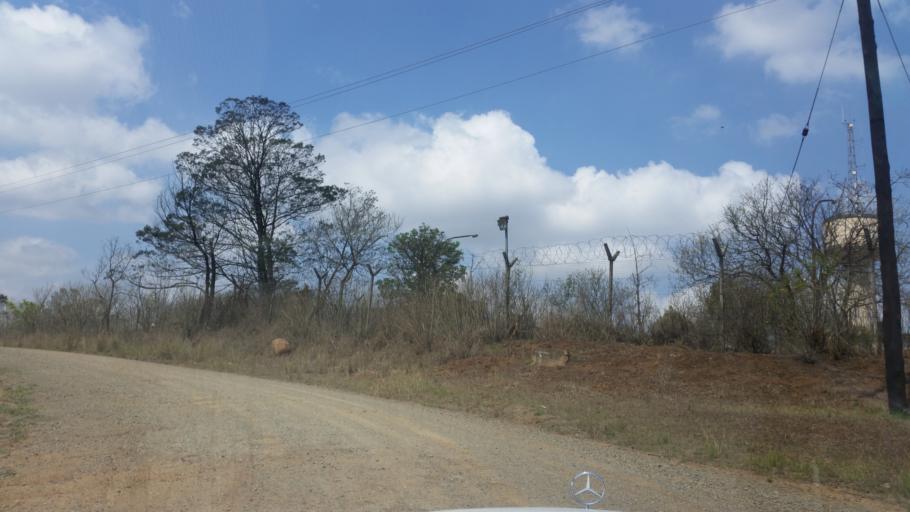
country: ZA
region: KwaZulu-Natal
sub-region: uMgungundlovu District Municipality
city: Camperdown
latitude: -29.7133
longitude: 30.4975
